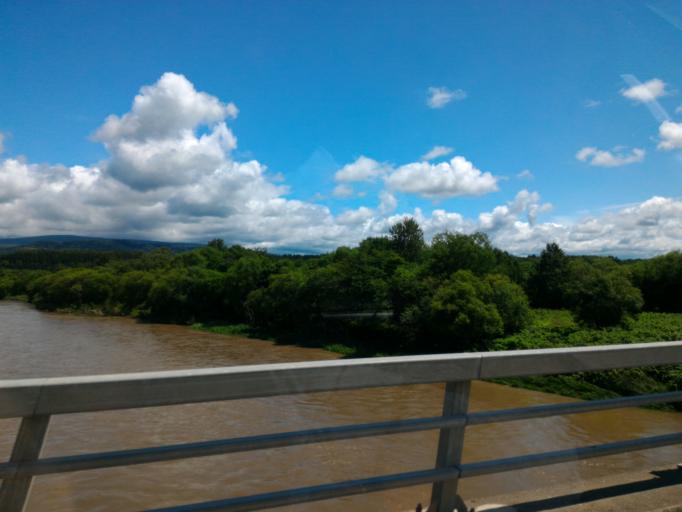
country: JP
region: Hokkaido
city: Nayoro
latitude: 44.5262
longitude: 142.3256
